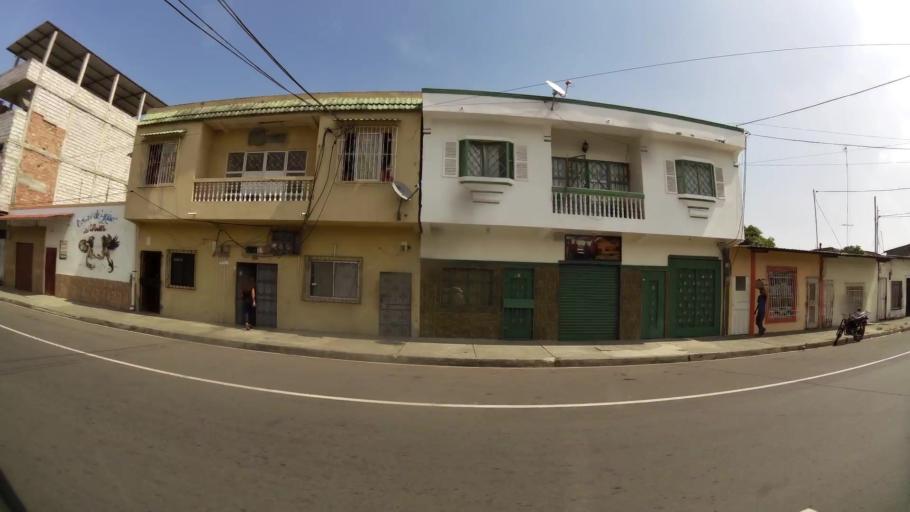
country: EC
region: Guayas
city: Eloy Alfaro
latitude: -2.1614
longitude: -79.8433
